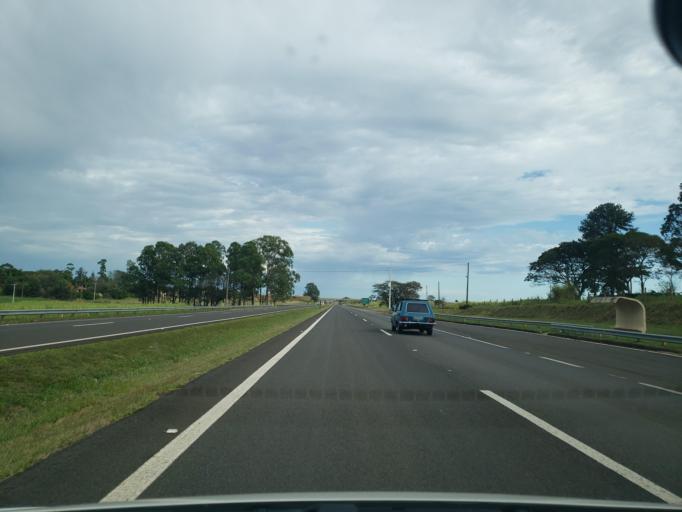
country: BR
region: Sao Paulo
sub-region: Dois Corregos
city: Dois Corregos
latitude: -22.2655
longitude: -48.4352
